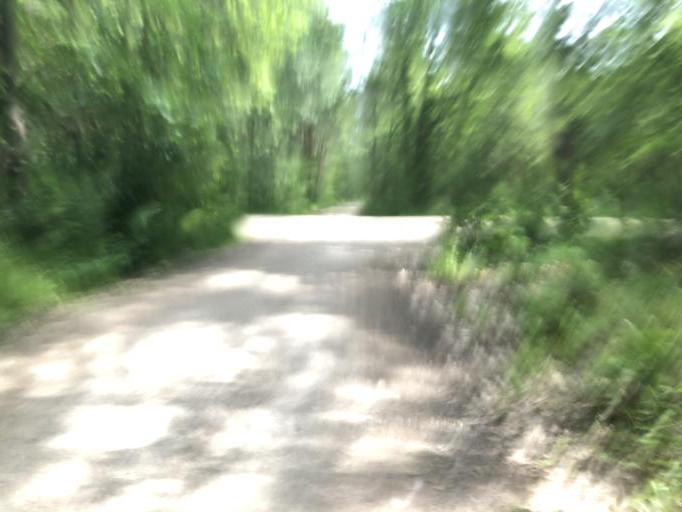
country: DE
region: Bavaria
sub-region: Regierungsbezirk Mittelfranken
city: Mohrendorf
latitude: 49.6106
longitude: 10.9654
